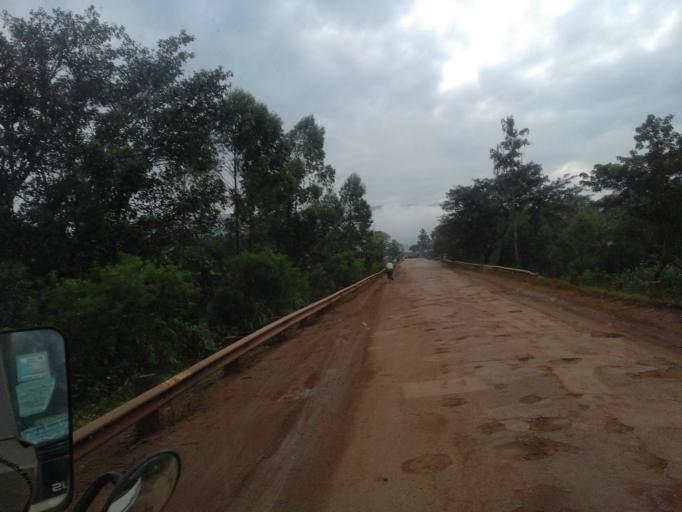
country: UG
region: Eastern Region
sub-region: Sironko District
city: Sironko
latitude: 1.2363
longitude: 34.2571
